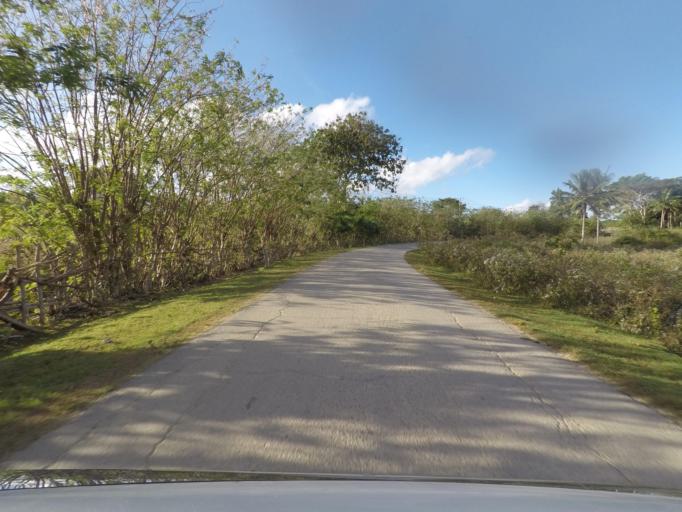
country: TL
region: Lautem
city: Lospalos
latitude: -8.4579
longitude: 126.9996
